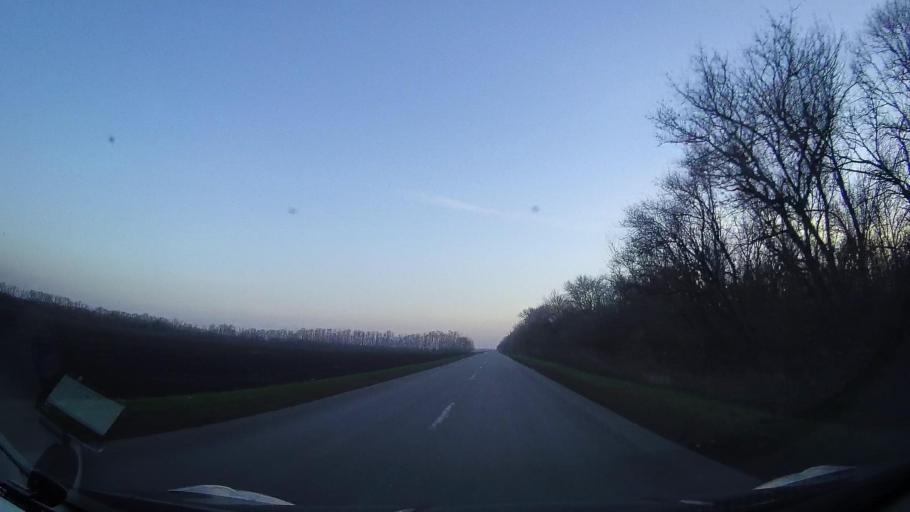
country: RU
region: Rostov
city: Zernograd
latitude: 46.9934
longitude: 40.3915
